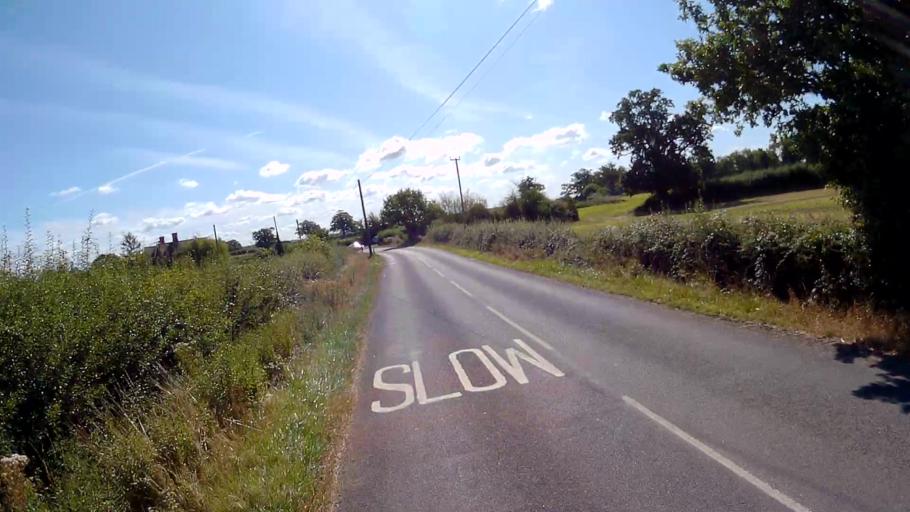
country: GB
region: England
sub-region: West Berkshire
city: Stratfield Mortimer
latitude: 51.3683
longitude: -1.0273
